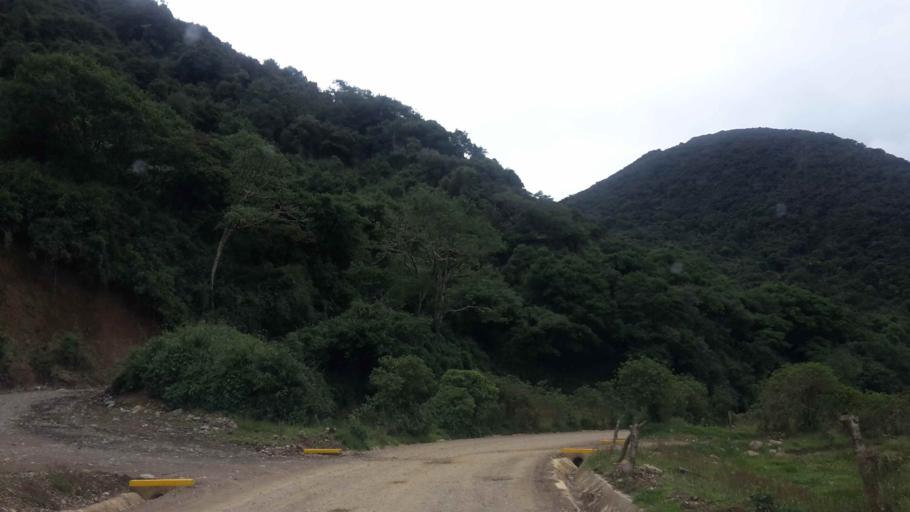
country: BO
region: Cochabamba
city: Totora
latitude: -17.5629
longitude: -65.2757
